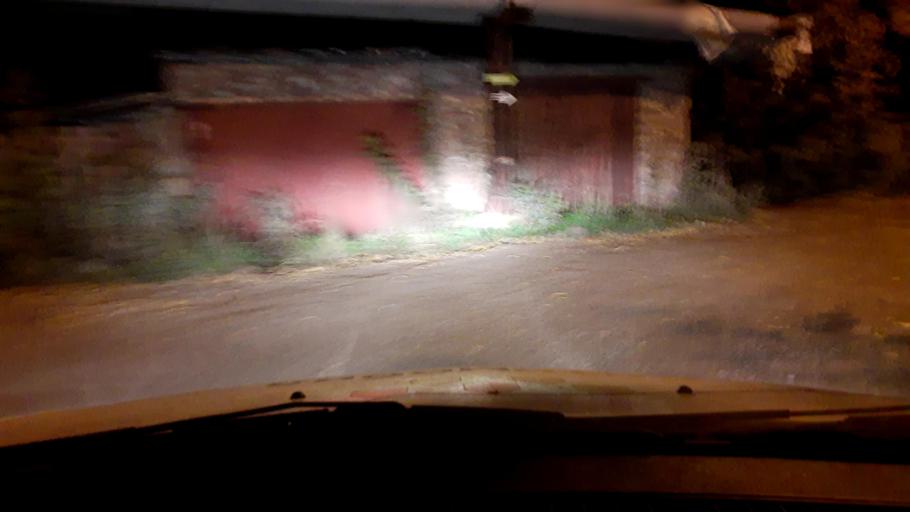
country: RU
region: Bashkortostan
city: Ufa
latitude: 54.8322
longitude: 56.0670
